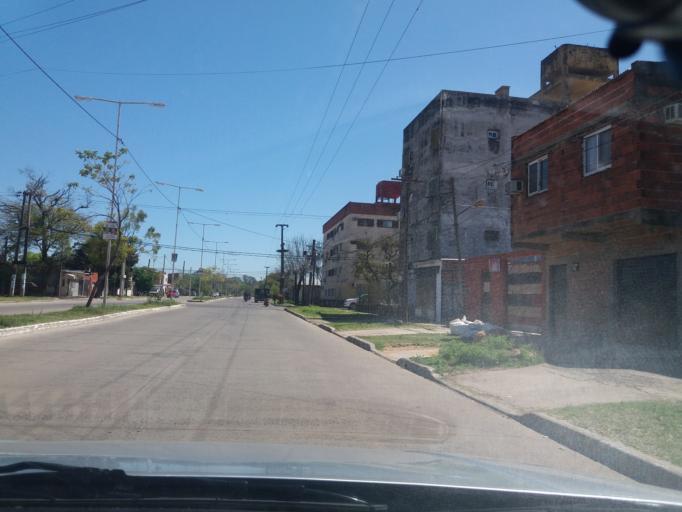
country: AR
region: Corrientes
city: Corrientes
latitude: -27.4884
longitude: -58.8435
